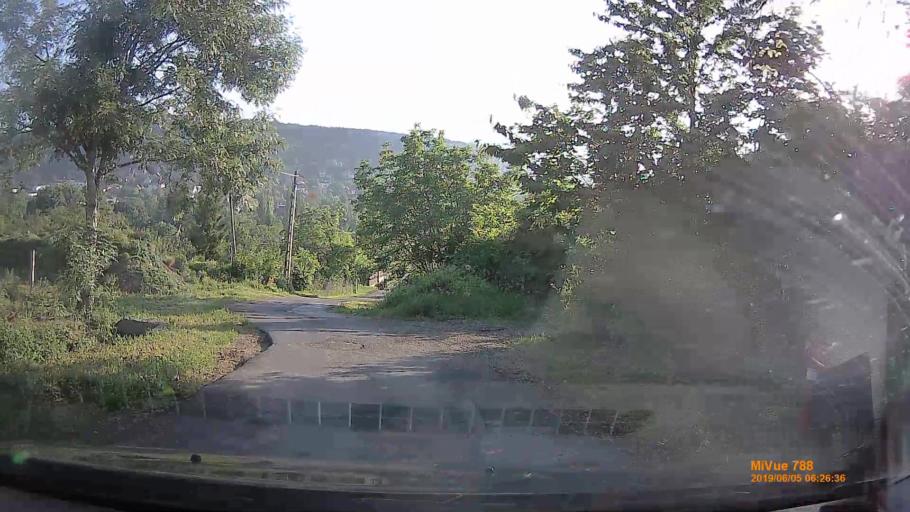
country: HU
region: Pest
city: Urom
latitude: 47.5779
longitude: 19.0276
